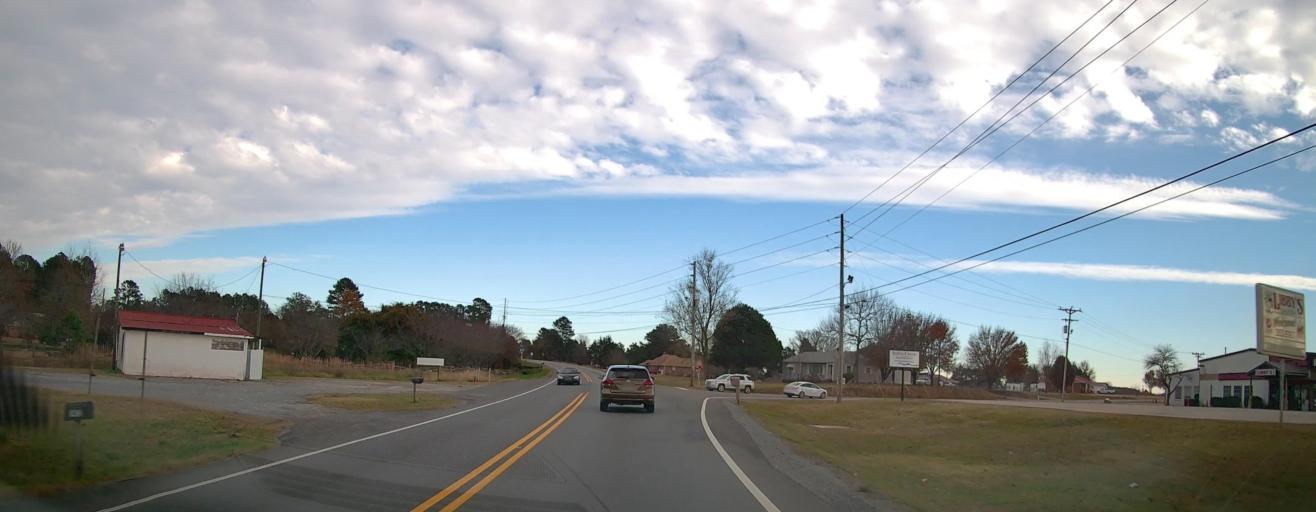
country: US
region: Alabama
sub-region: Morgan County
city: Priceville
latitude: 34.5062
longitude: -86.8693
